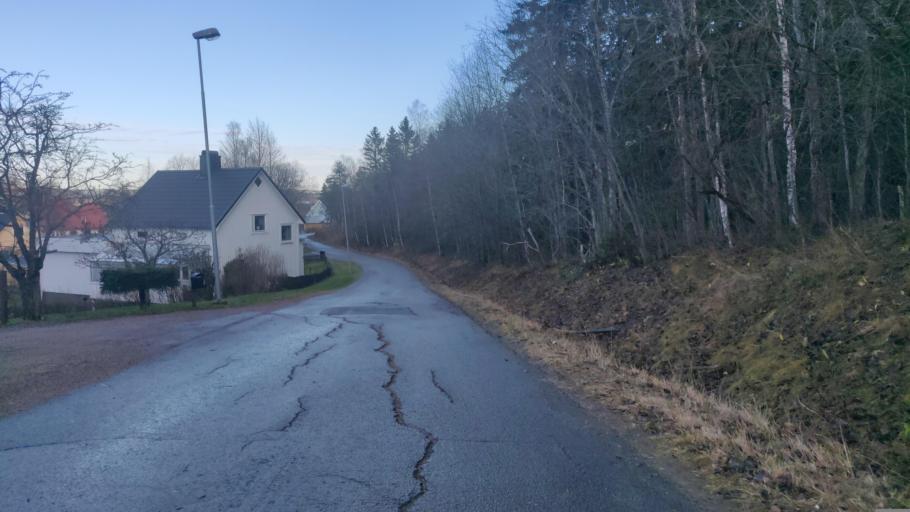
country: SE
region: Vaesternorrland
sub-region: Sundsvalls Kommun
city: Kvissleby
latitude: 62.3091
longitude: 17.3645
